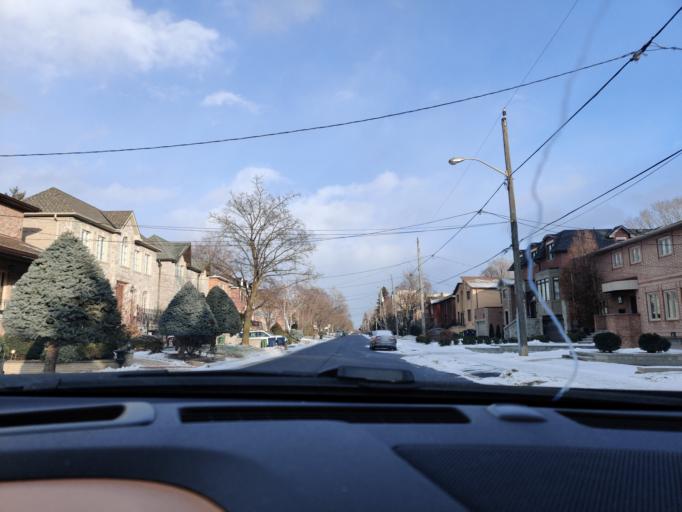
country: CA
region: Ontario
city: Toronto
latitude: 43.7161
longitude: -79.4371
